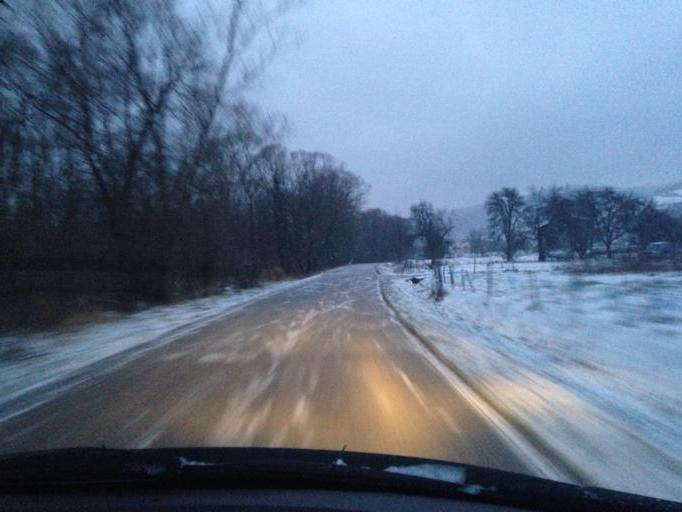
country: PL
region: Subcarpathian Voivodeship
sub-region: Powiat jasielski
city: Krempna
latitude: 49.5316
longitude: 21.5517
